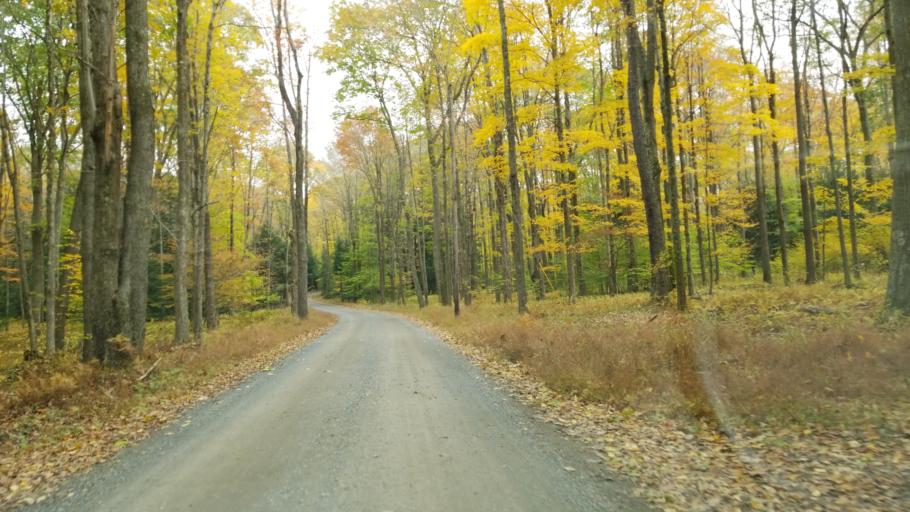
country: US
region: Pennsylvania
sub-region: Clearfield County
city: Clearfield
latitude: 41.1984
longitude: -78.4162
